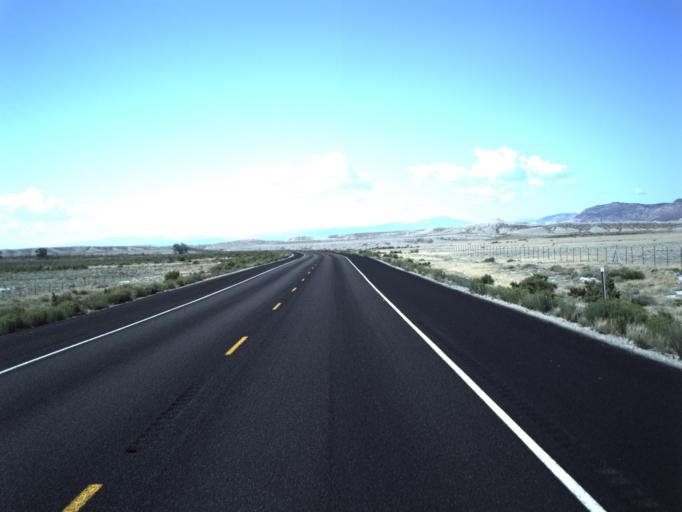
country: US
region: Utah
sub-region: Emery County
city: Ferron
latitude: 38.9981
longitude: -111.1629
